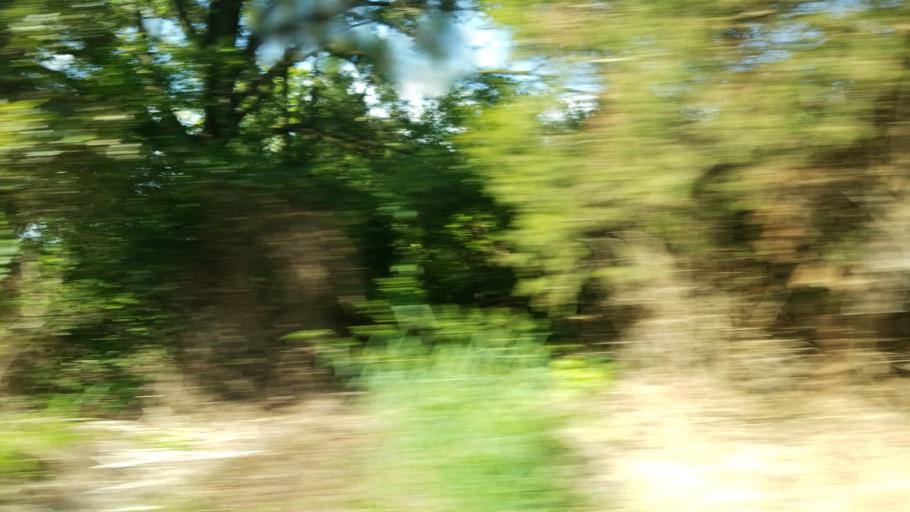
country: US
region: Illinois
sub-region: Saline County
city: Harrisburg
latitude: 37.8127
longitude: -88.5571
